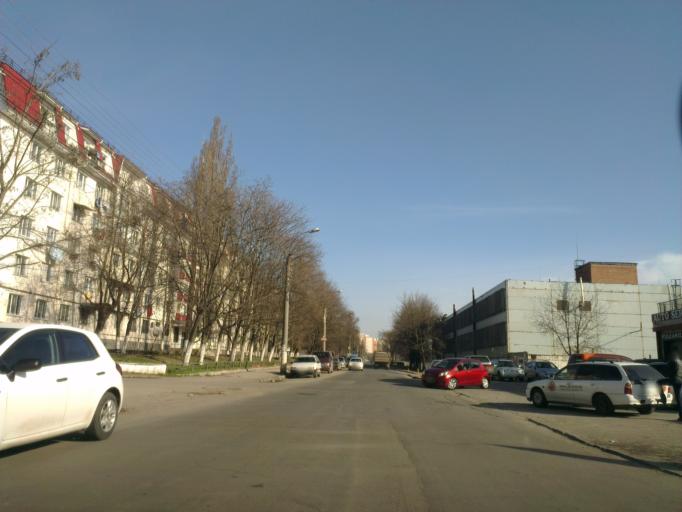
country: MD
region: Chisinau
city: Chisinau
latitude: 47.0236
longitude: 28.8833
